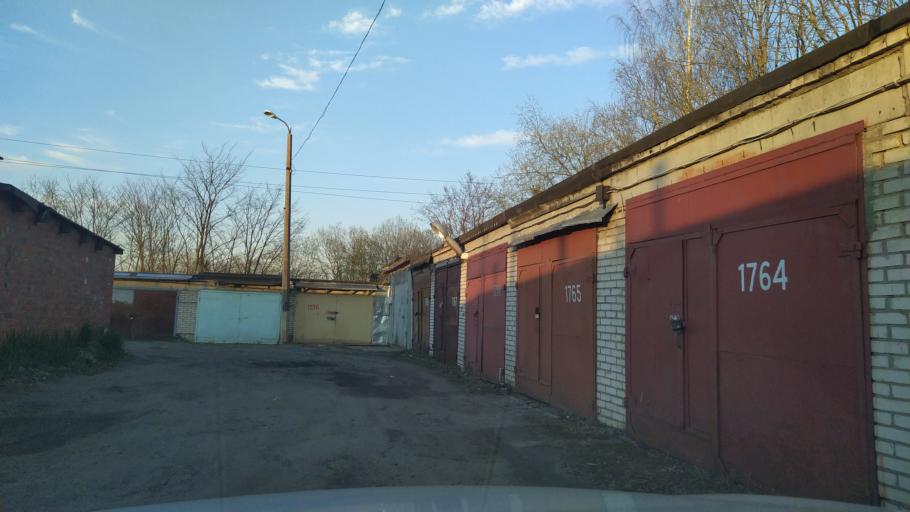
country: RU
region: St.-Petersburg
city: Pushkin
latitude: 59.6912
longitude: 30.3959
